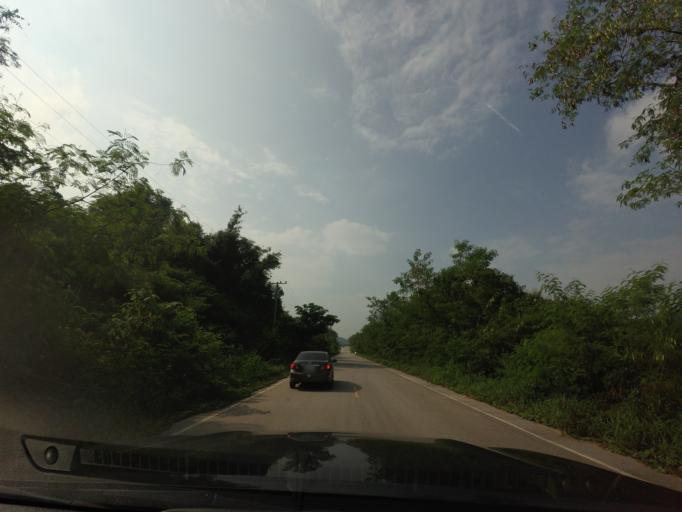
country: TH
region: Loei
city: Chiang Khan
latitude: 17.8612
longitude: 101.5731
